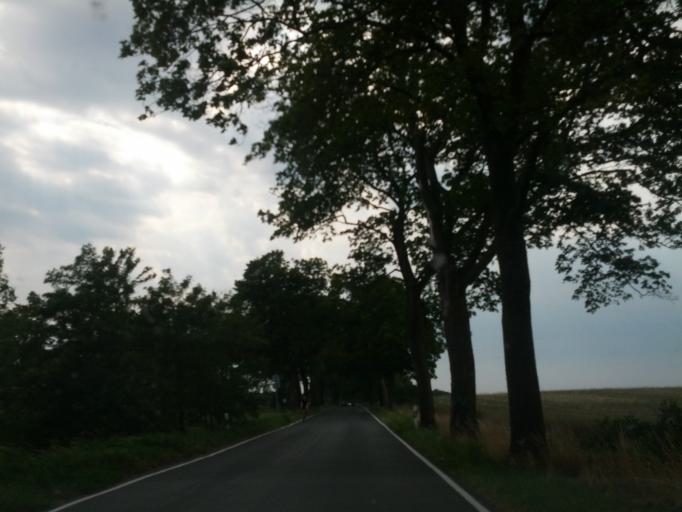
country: DE
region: Brandenburg
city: Kremmen
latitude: 52.7472
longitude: 12.9458
